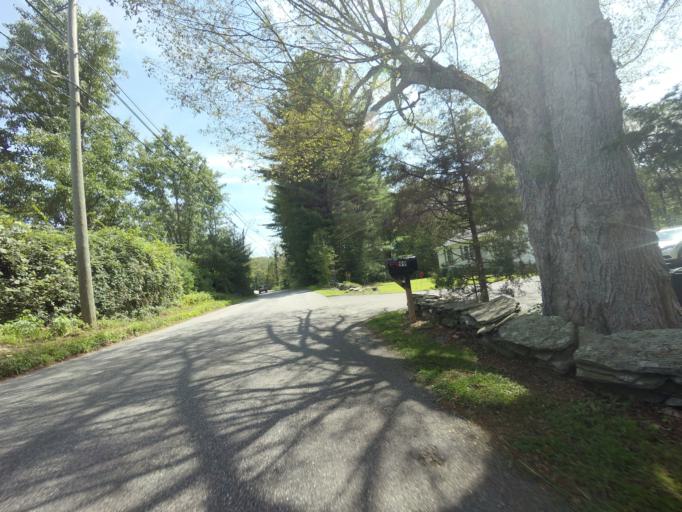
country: US
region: Connecticut
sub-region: Windham County
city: East Brooklyn
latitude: 41.8261
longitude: -71.9326
